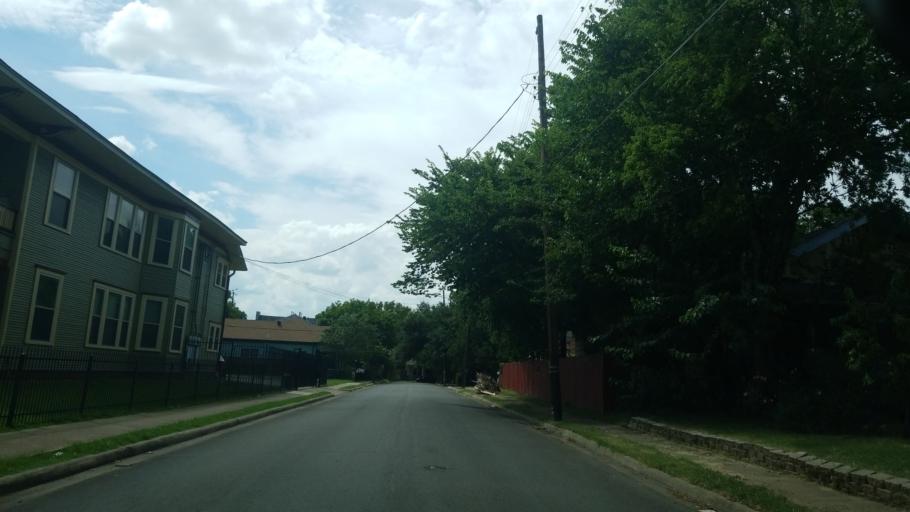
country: US
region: Texas
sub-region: Dallas County
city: Dallas
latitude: 32.7954
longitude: -96.7660
